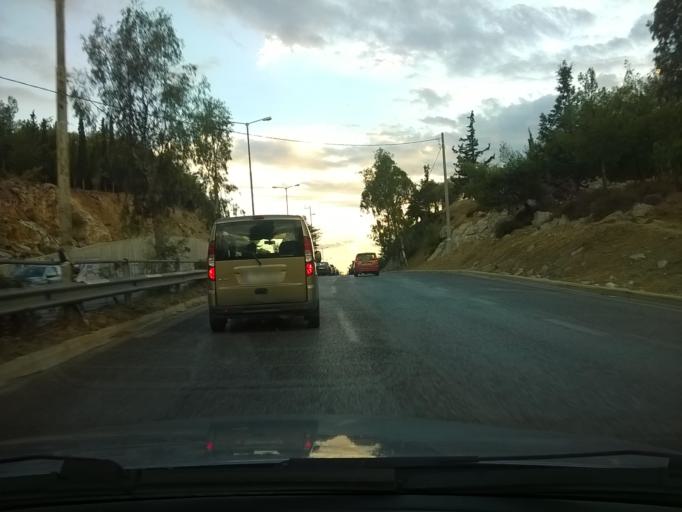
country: GR
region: Attica
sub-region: Nomarchia Athinas
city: Kaisariani
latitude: 37.9557
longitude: 23.7745
